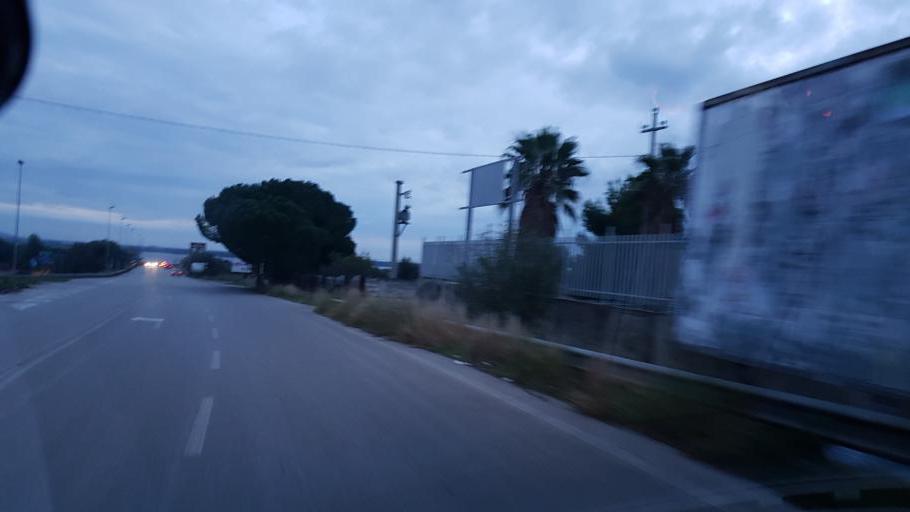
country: IT
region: Apulia
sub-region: Provincia di Taranto
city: Paolo VI
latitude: 40.5138
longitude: 17.2887
